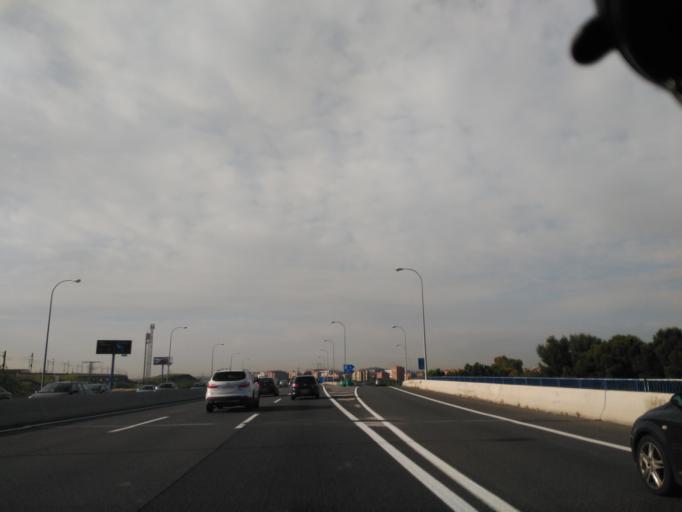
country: ES
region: Madrid
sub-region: Provincia de Madrid
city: Villaverde
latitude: 40.3662
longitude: -3.6784
